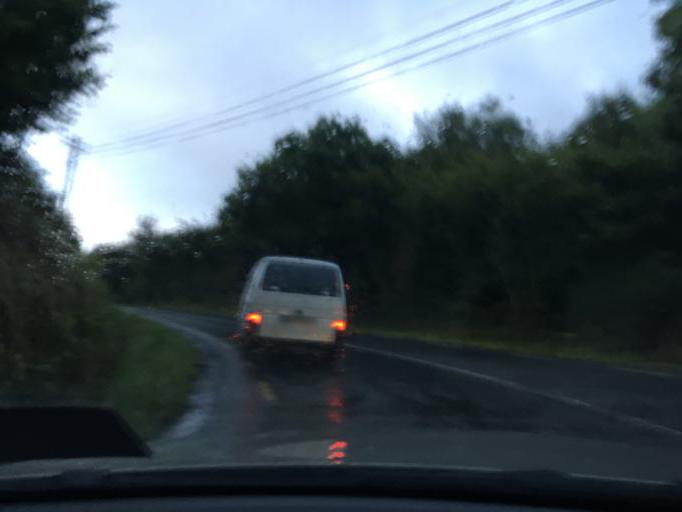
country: IE
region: Ulster
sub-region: County Donegal
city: Killybegs
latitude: 54.6349
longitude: -8.4734
